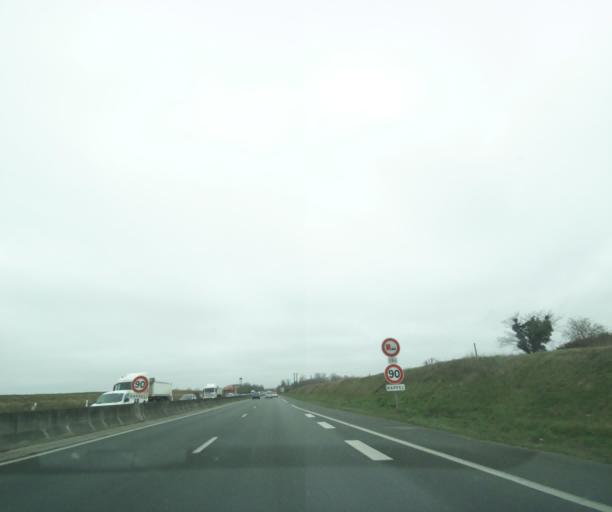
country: FR
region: Poitou-Charentes
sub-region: Departement de la Charente-Maritime
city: Aytre
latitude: 46.1437
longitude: -1.1076
